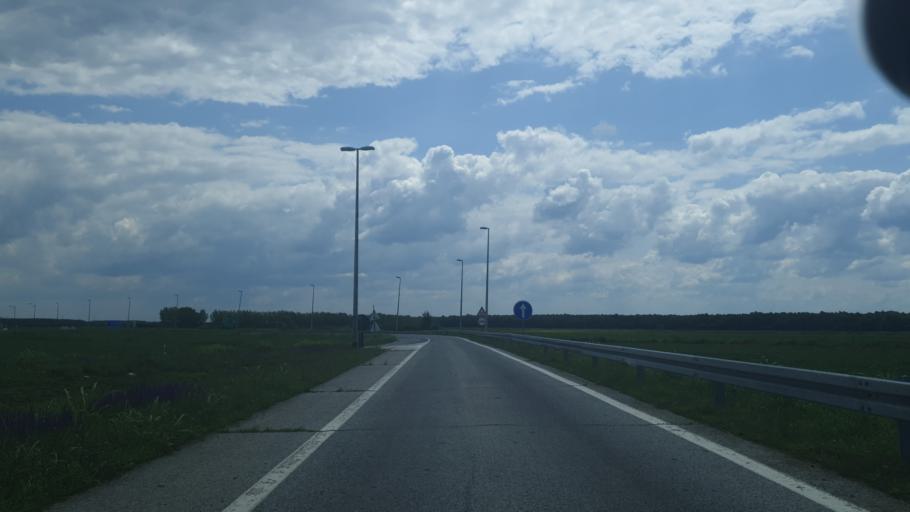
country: RS
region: Autonomna Pokrajina Vojvodina
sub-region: Sremski Okrug
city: Sid
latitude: 45.0470
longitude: 19.2057
